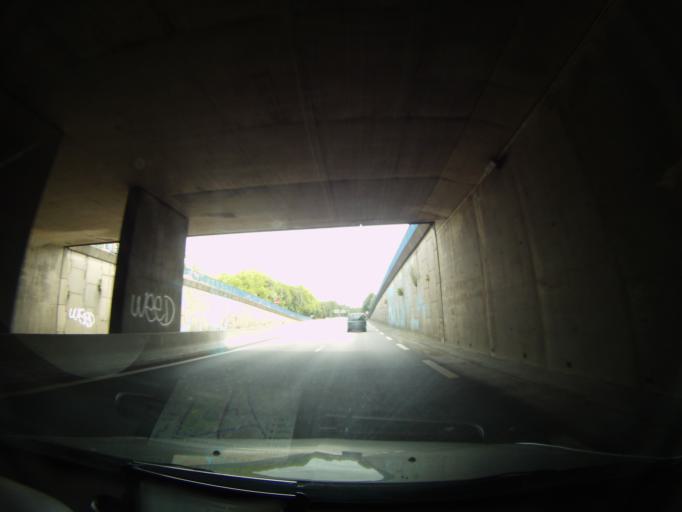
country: FR
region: Pays de la Loire
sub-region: Departement de la Loire-Atlantique
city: Nantes
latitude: 47.2549
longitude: -1.5297
